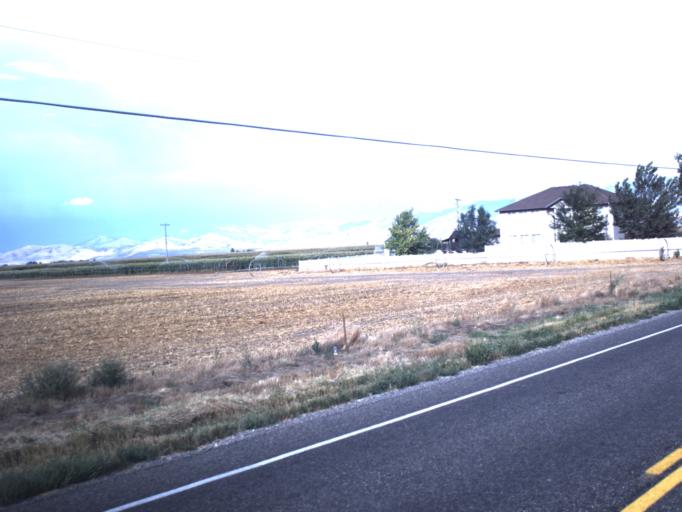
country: US
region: Utah
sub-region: Cache County
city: Lewiston
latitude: 41.9754
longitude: -111.9168
